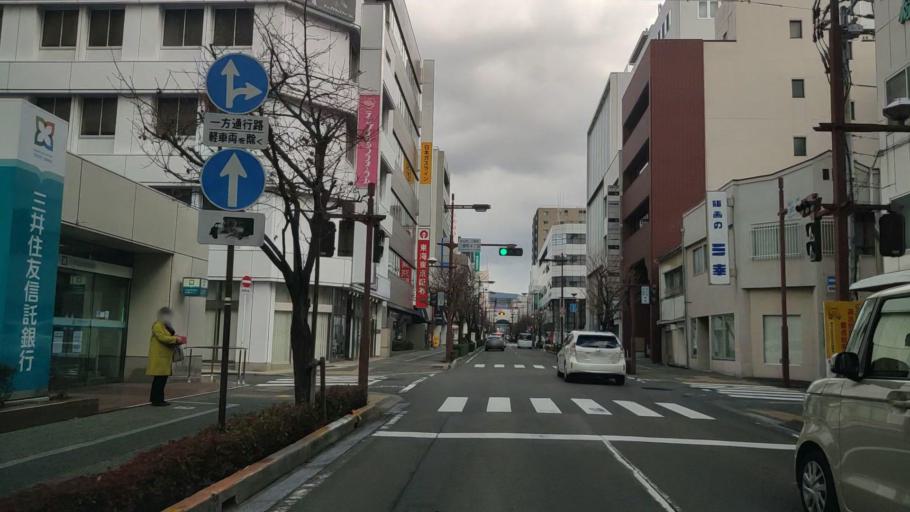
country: JP
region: Ehime
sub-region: Shikoku-chuo Shi
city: Matsuyama
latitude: 33.8383
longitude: 132.7667
